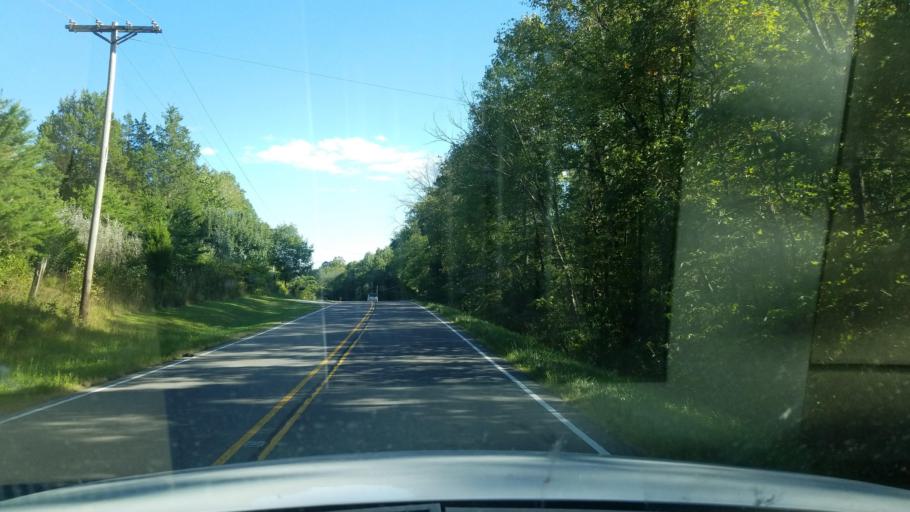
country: US
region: Illinois
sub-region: Saline County
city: Harrisburg
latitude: 37.6075
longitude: -88.4628
